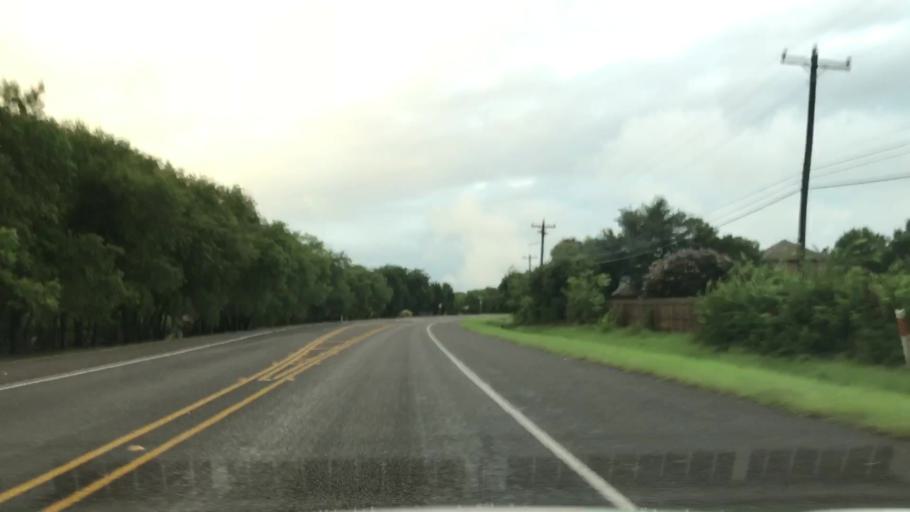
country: US
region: Texas
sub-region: Rockwall County
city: Rockwall
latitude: 32.9703
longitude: -96.4654
